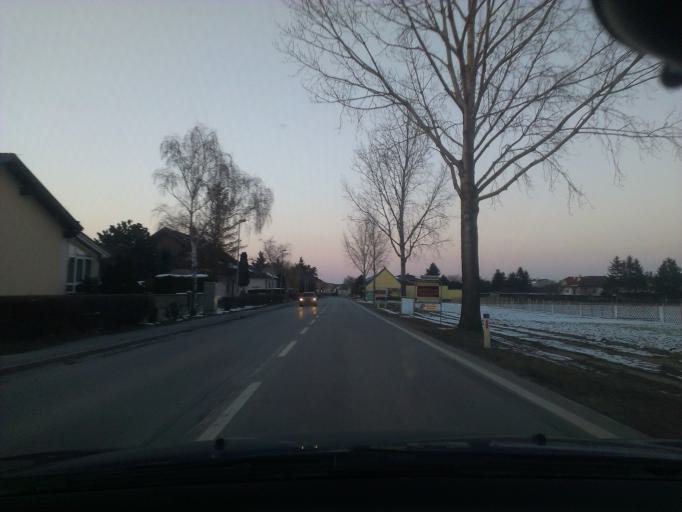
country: AT
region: Lower Austria
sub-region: Politischer Bezirk Bruck an der Leitha
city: Enzersdorf an der Fischa
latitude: 48.0757
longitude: 16.6085
